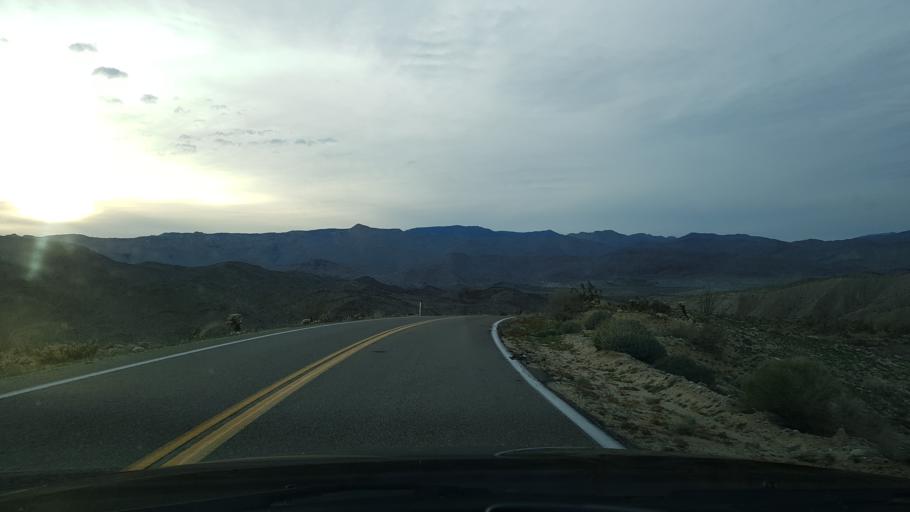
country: MX
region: Baja California
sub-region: Tecate
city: Cereso del Hongo
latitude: 32.8310
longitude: -116.1735
